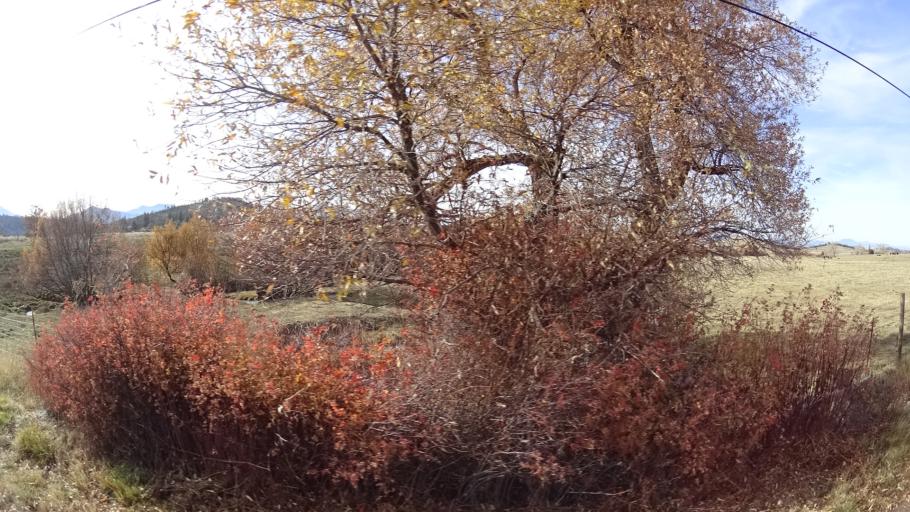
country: US
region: California
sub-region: Siskiyou County
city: Weed
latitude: 41.4584
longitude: -122.3845
